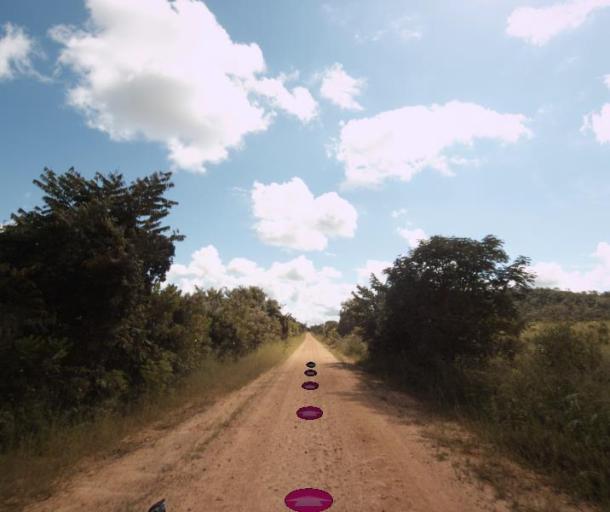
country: BR
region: Goias
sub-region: Pirenopolis
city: Pirenopolis
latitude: -15.7744
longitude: -48.9988
